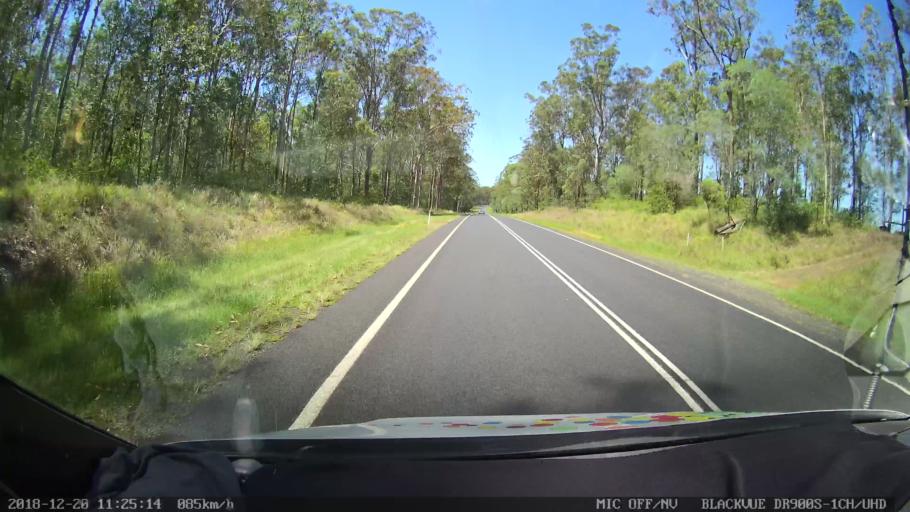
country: AU
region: New South Wales
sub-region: Richmond Valley
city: Casino
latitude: -29.0849
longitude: 153.0007
